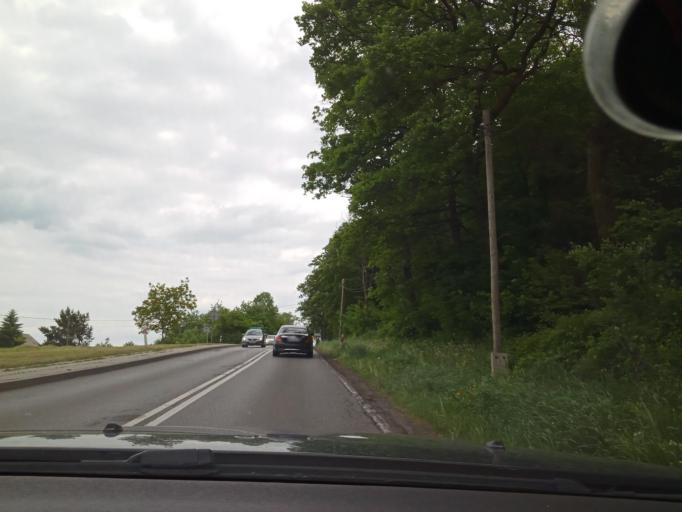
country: PL
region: Lesser Poland Voivodeship
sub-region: Powiat wielicki
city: Tomaszkowice
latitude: 49.9729
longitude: 20.1159
